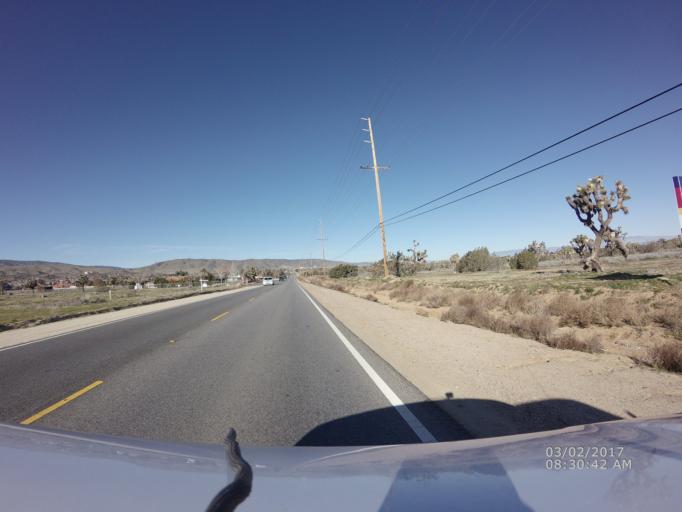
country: US
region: California
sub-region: Los Angeles County
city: Quartz Hill
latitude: 34.6311
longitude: -118.1953
